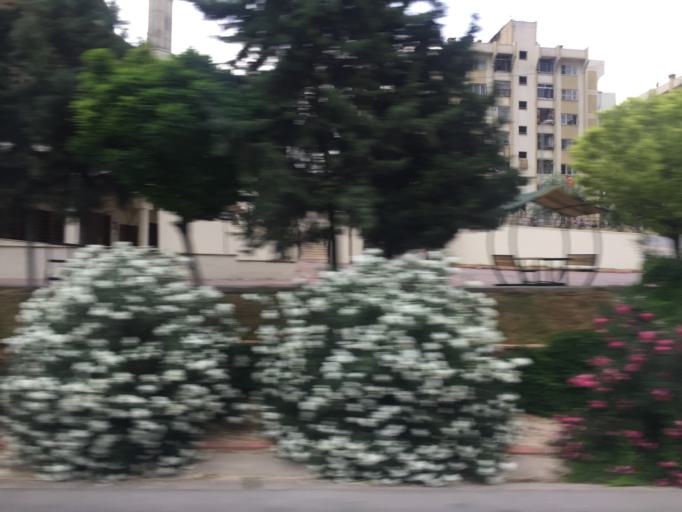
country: TR
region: Gaziantep
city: Gaziantep
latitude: 37.0461
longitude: 37.4242
